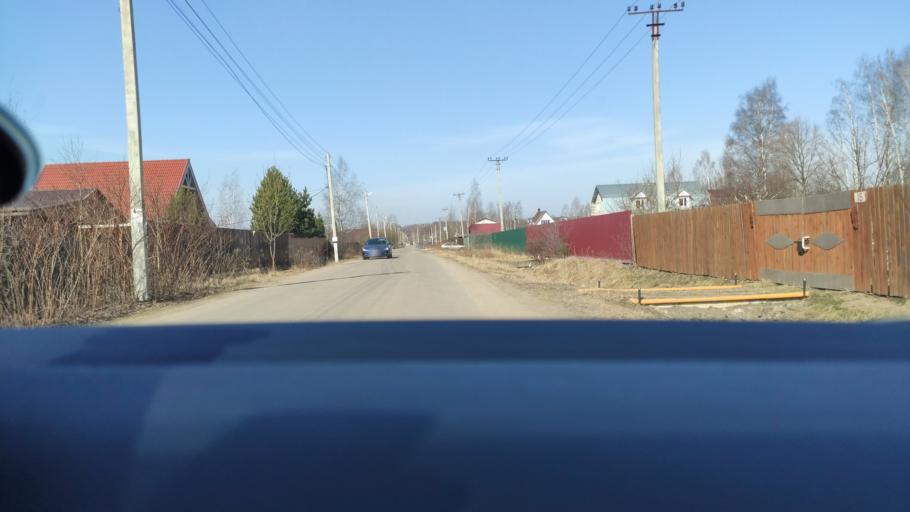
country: RU
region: Moskovskaya
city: Imeni Vorovskogo
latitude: 55.7783
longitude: 38.3707
